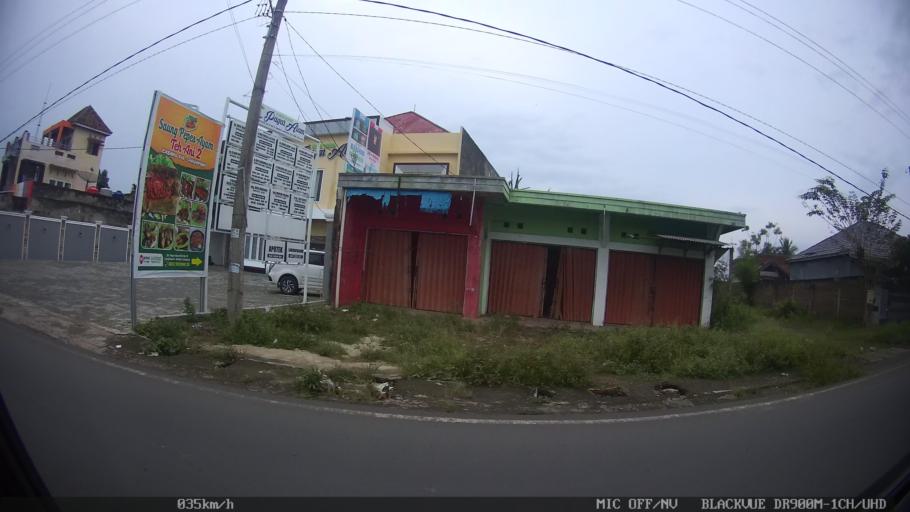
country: ID
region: Lampung
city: Kedaton
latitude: -5.3891
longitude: 105.2398
